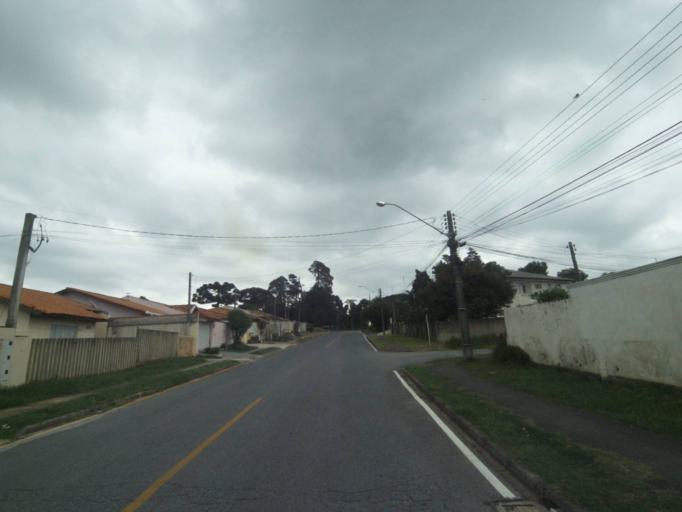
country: BR
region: Parana
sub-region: Quatro Barras
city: Quatro Barras
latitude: -25.3522
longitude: -49.1194
